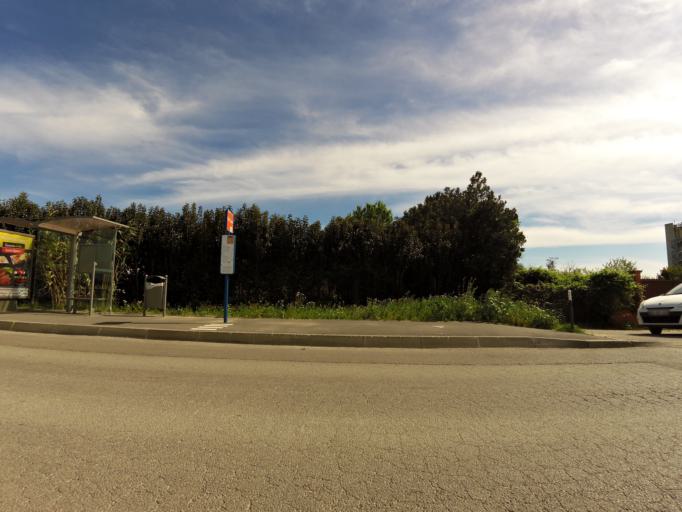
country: FR
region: Languedoc-Roussillon
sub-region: Departement de l'Herault
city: Saint-Just
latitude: 43.6648
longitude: 4.1265
